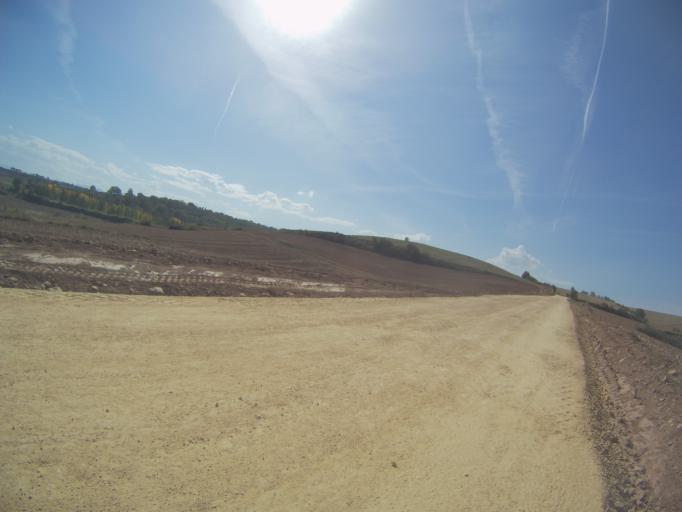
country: ES
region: La Rioja
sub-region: Provincia de La Rioja
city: Ciruena
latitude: 42.4249
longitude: -2.8738
